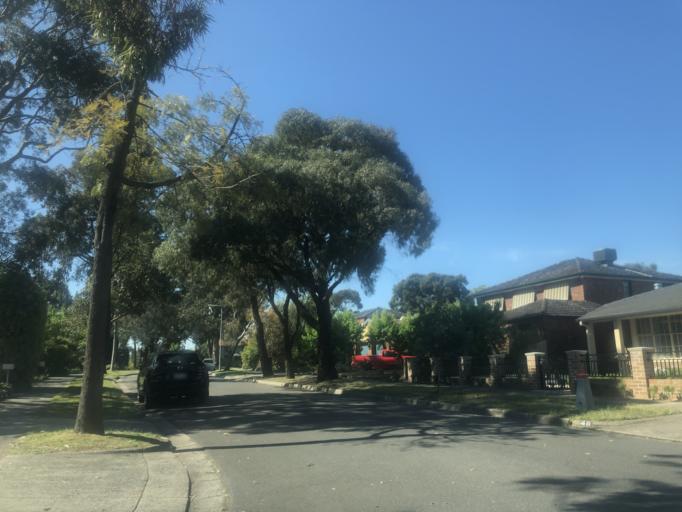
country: AU
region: Victoria
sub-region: Monash
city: Mulgrave
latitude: -37.9056
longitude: 145.1863
